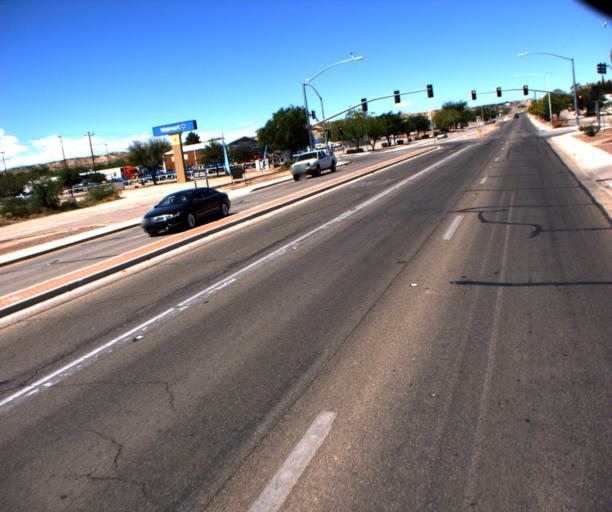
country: US
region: Arizona
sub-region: Cochise County
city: Benson
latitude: 31.9710
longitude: -110.3131
